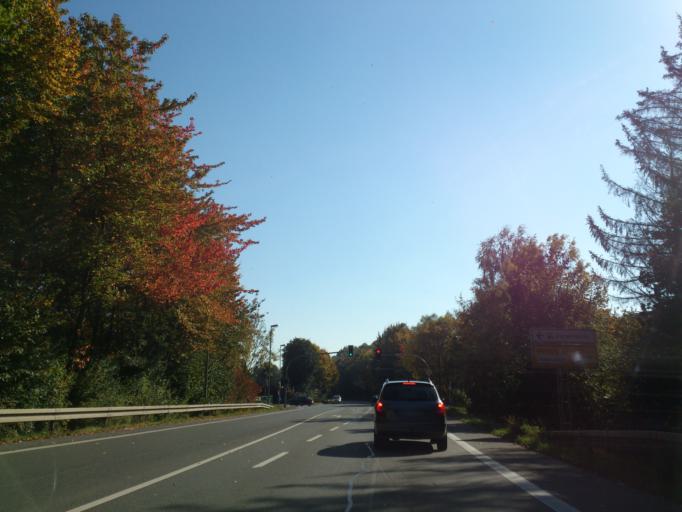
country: DE
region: North Rhine-Westphalia
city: Warburg
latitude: 51.4920
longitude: 9.1455
